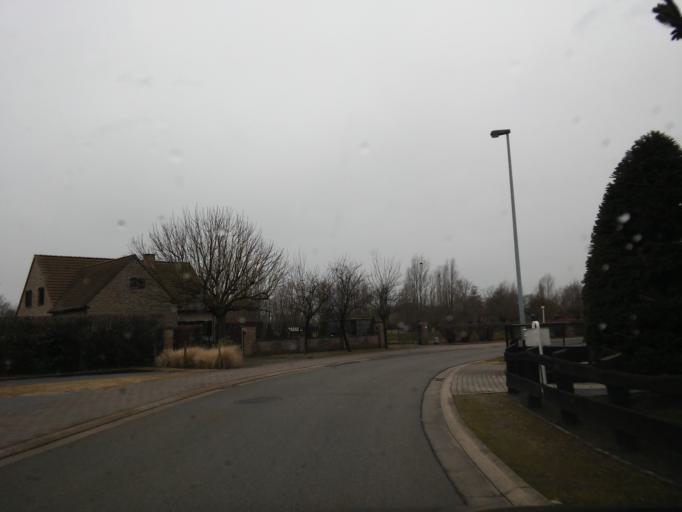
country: BE
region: Flanders
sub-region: Provincie Oost-Vlaanderen
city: Hamme
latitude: 51.0924
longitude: 4.1666
